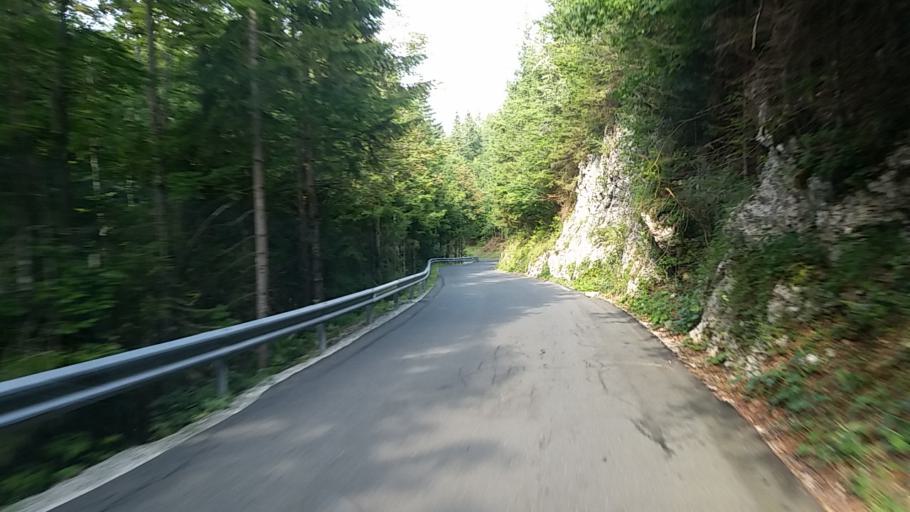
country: SI
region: Bohinj
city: Bohinjska Bistrica
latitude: 46.2711
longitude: 14.0193
